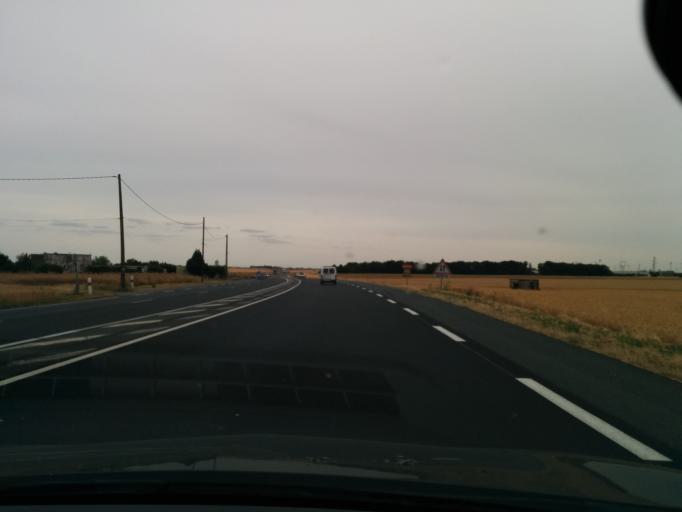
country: FR
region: Ile-de-France
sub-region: Departement de l'Essonne
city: Angerville
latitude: 48.2897
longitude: 1.9820
